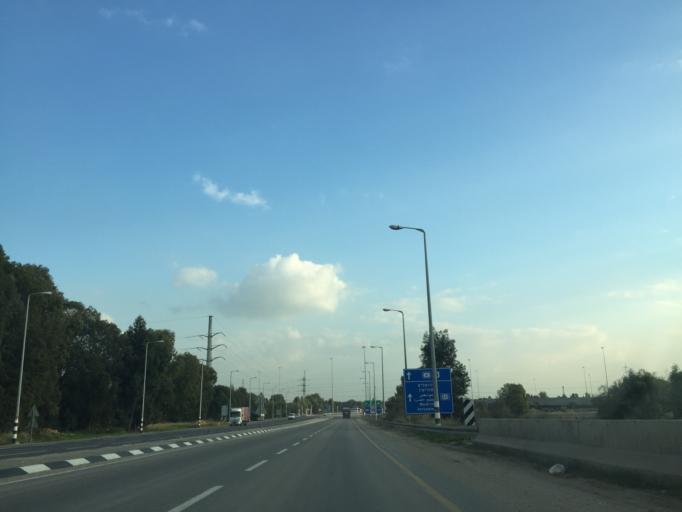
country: IL
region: Central District
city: Ramla
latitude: 31.9155
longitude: 34.8881
